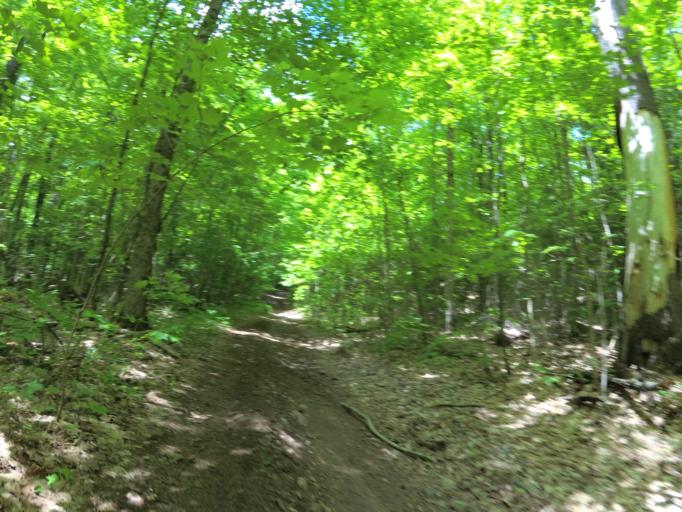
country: CA
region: Ontario
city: Renfrew
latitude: 45.0599
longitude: -76.8575
